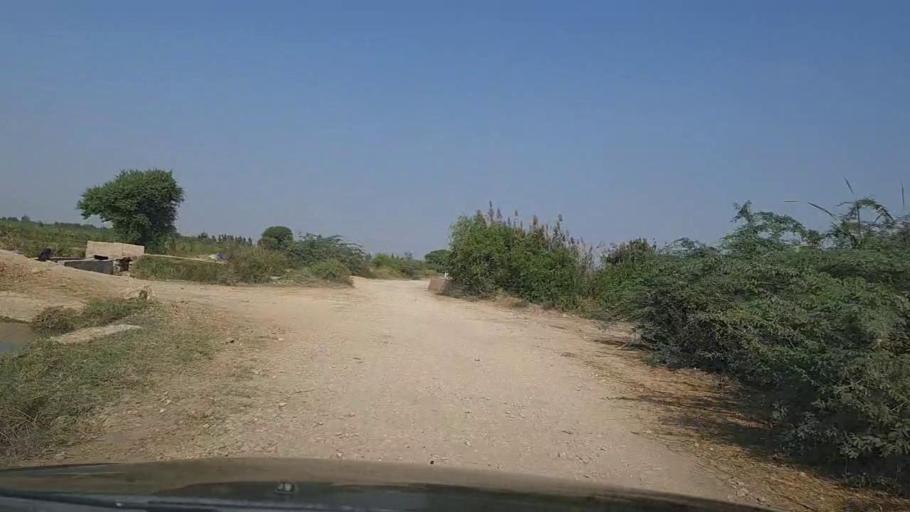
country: PK
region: Sindh
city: Thatta
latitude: 24.6299
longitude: 67.8137
